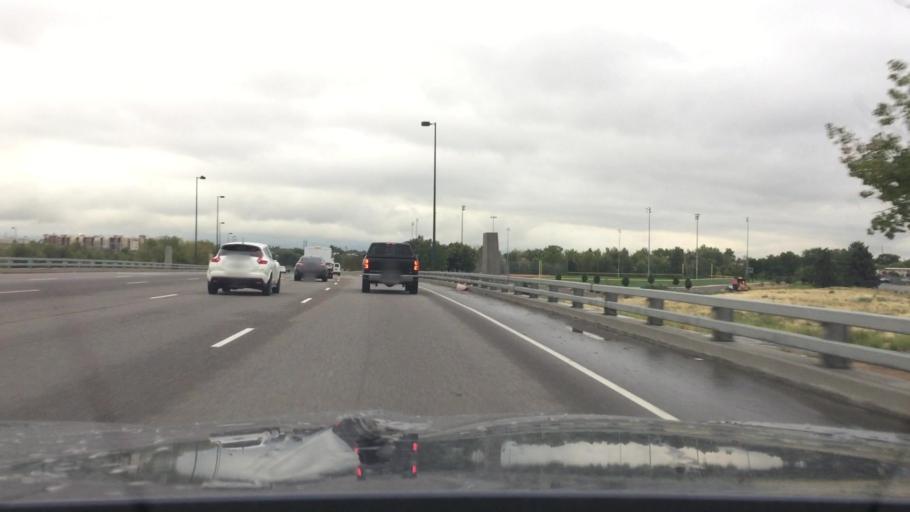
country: US
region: Colorado
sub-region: Denver County
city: Denver
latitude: 39.7038
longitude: -104.9964
